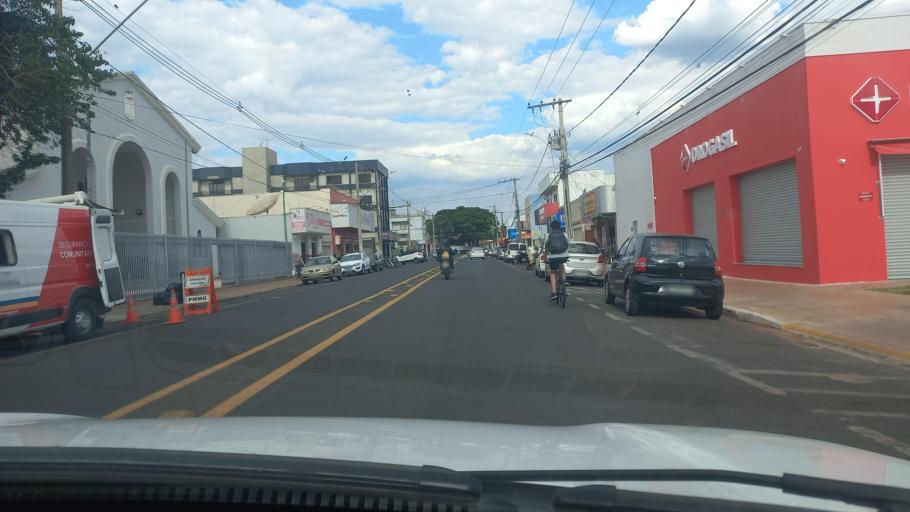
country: BR
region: Minas Gerais
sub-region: Uberaba
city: Uberaba
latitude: -19.7345
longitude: -47.9222
